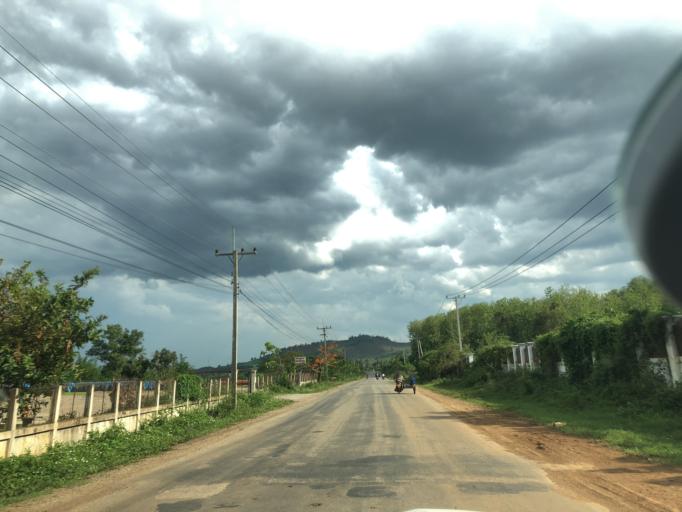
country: TH
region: Uttaradit
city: Ban Khok
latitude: 18.1464
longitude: 101.3820
